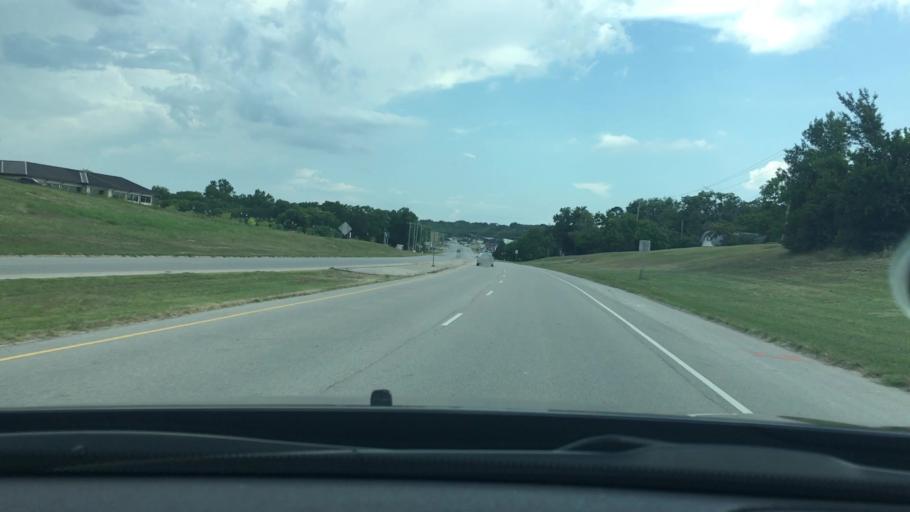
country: US
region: Oklahoma
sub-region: Pontotoc County
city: Ada
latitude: 34.7544
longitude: -96.6582
